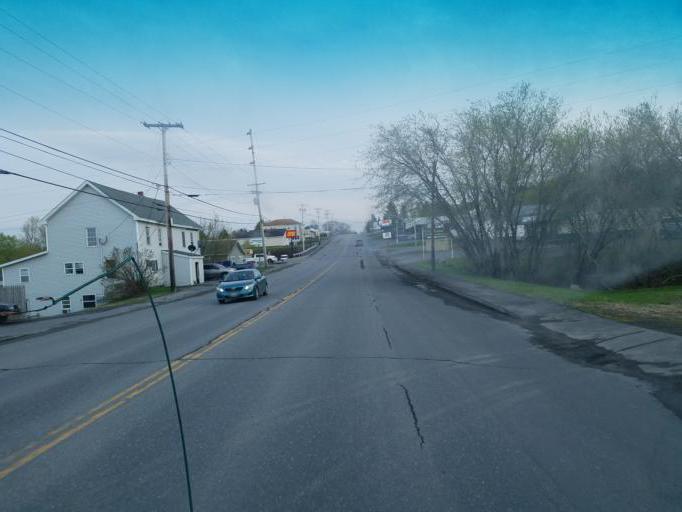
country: US
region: Maine
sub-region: Aroostook County
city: Caribou
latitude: 46.8513
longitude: -68.0110
